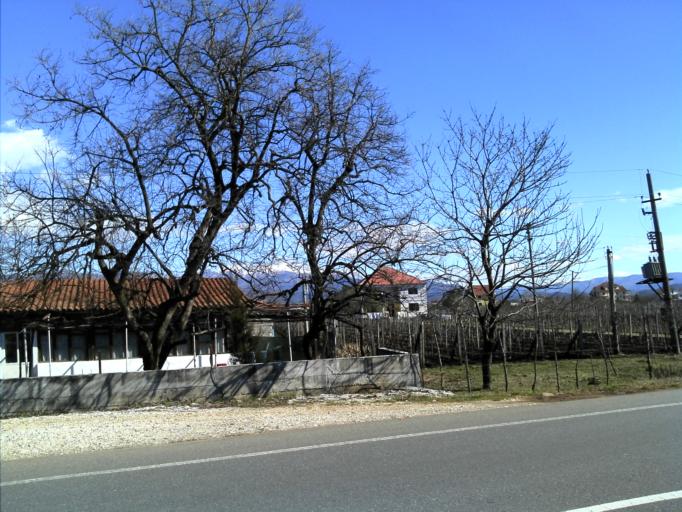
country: AL
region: Shkoder
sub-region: Rrethi i Shkodres
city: Shkoder
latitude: 42.1103
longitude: 19.5011
